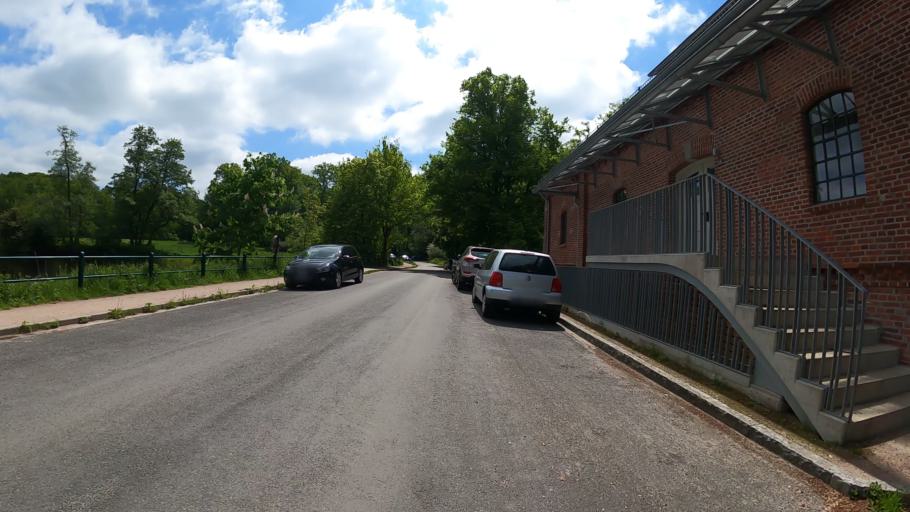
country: DE
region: Hamburg
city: Wohldorf-Ohlstedt
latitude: 53.7095
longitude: 10.1301
